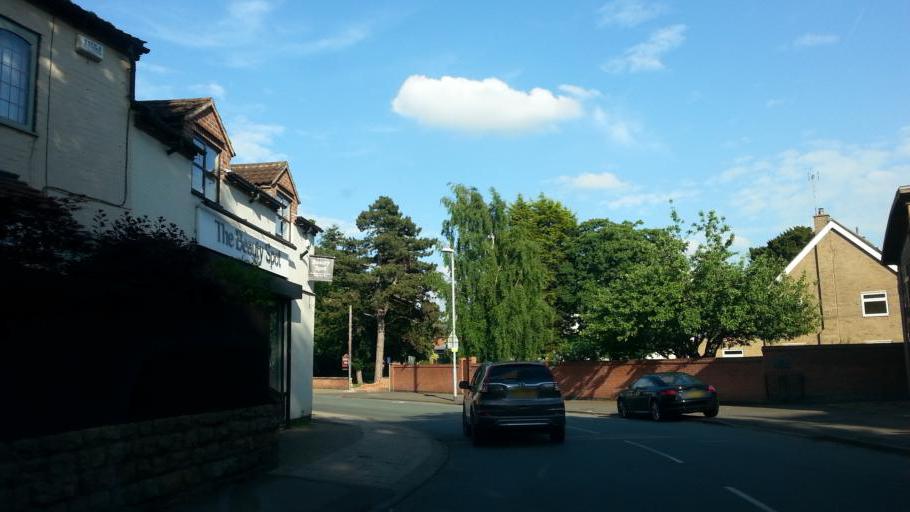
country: GB
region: England
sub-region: Nottinghamshire
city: Radcliffe on Trent
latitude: 52.9467
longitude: -1.0415
